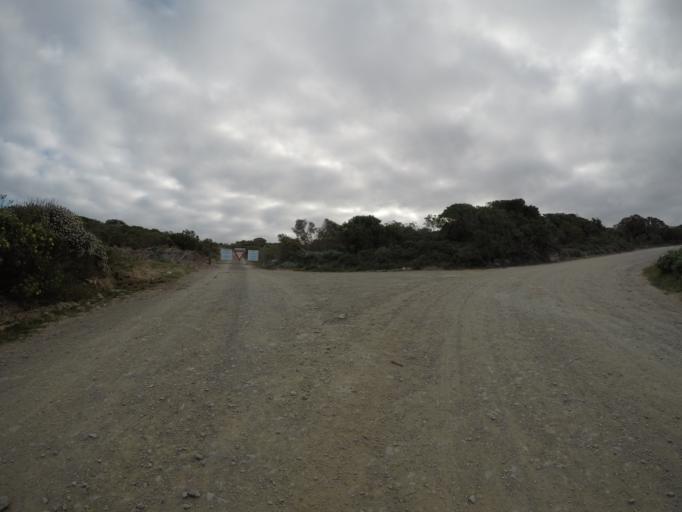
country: ZA
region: Western Cape
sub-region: Eden District Municipality
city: Riversdale
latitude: -34.4241
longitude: 21.3302
